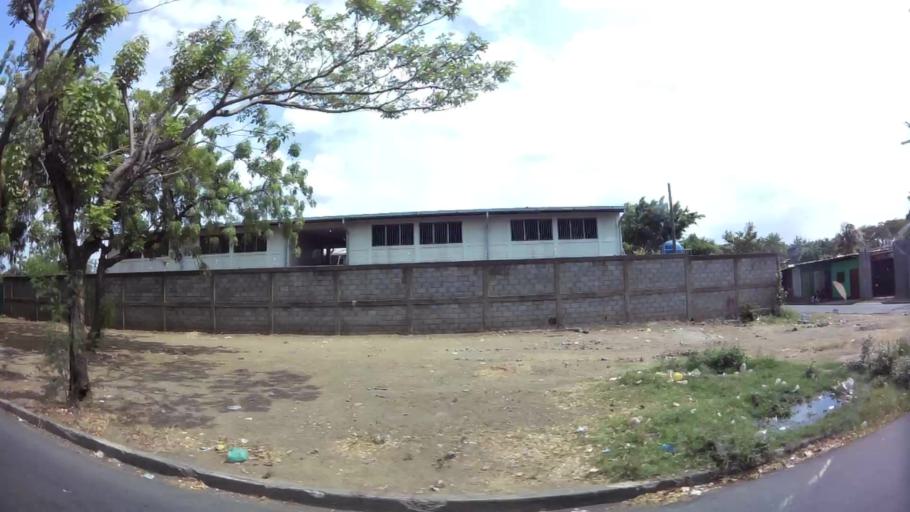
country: NI
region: Managua
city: Managua
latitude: 12.1505
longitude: -86.2689
